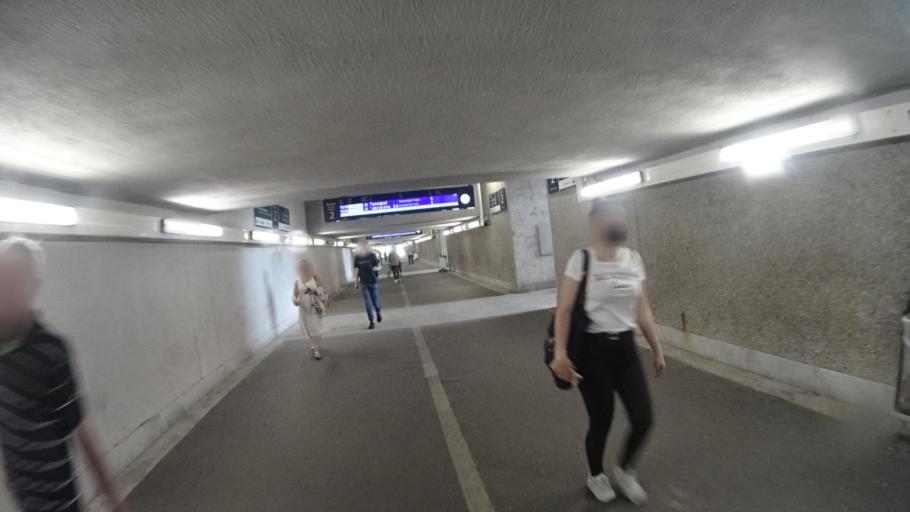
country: PL
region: Masovian Voivodeship
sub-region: Warszawa
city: Praga Polnoc
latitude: 52.2523
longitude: 21.0528
